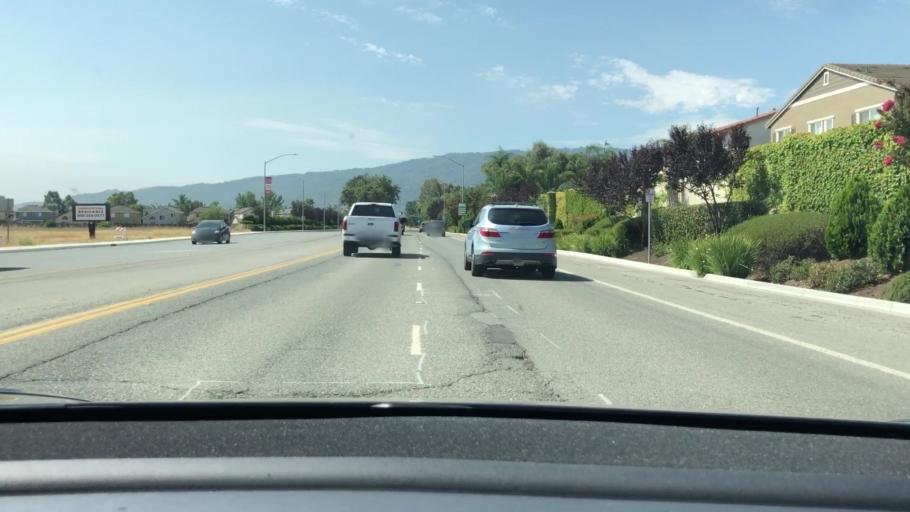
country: US
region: California
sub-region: Santa Clara County
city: Gilroy
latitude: 37.0313
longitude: -121.5979
